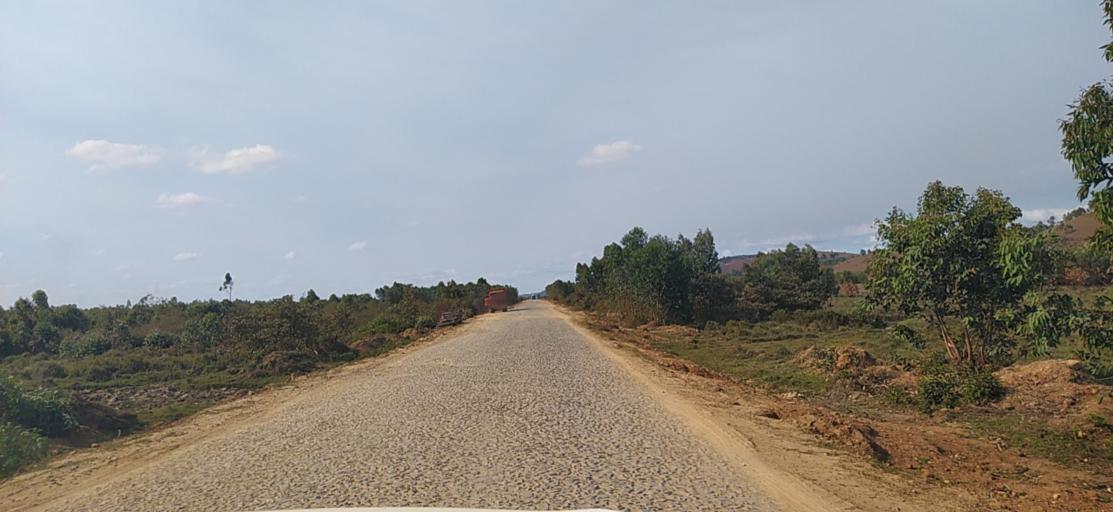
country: MG
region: Alaotra Mangoro
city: Moramanga
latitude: -18.6840
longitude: 48.2717
